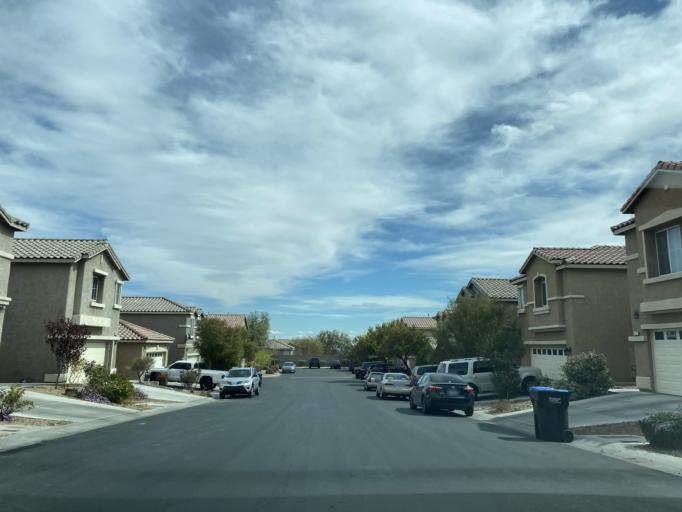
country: US
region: Nevada
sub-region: Clark County
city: Summerlin South
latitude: 36.3051
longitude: -115.3046
